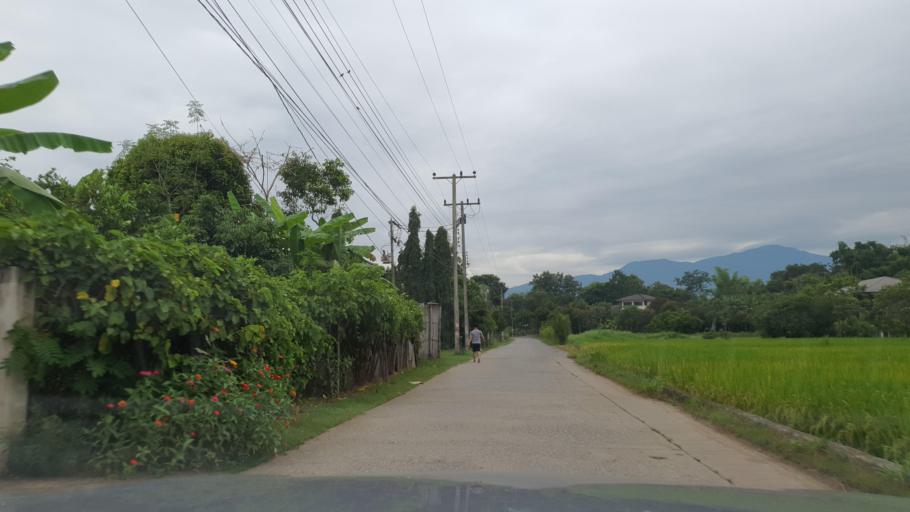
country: TH
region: Chiang Mai
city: San Sai
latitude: 18.9322
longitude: 98.9293
